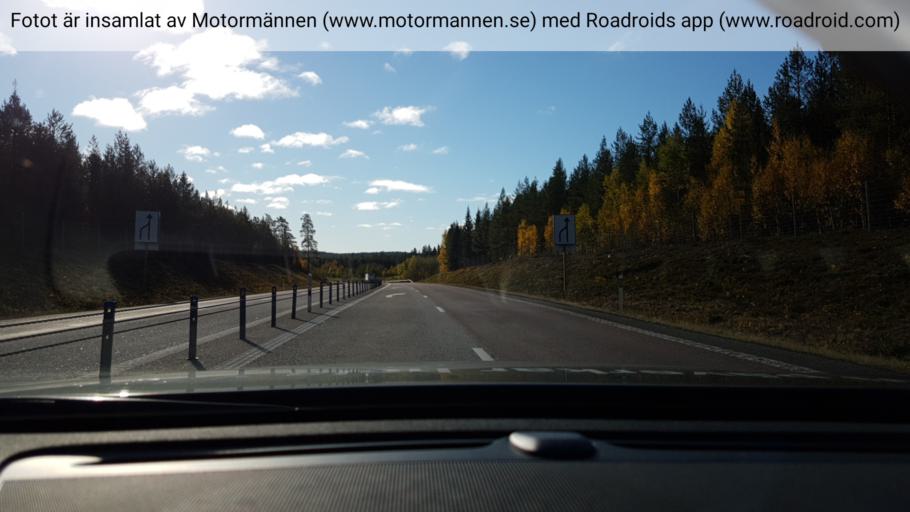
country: SE
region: Vaesterbotten
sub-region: Skelleftea Kommun
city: Skelleftea
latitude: 64.7094
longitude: 20.9963
